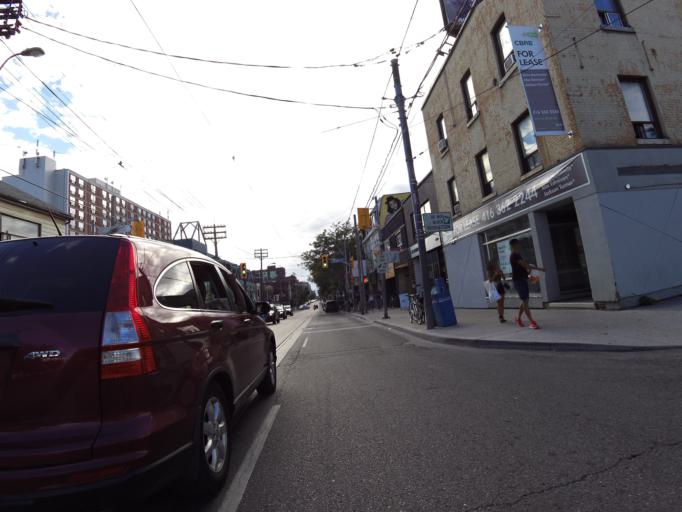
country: CA
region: Ontario
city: Toronto
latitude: 43.6461
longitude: -79.4095
